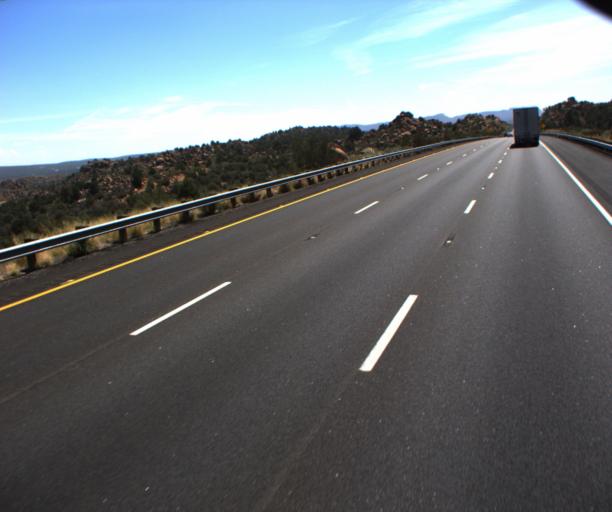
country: US
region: Arizona
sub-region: Mohave County
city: Peach Springs
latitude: 35.1852
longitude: -113.4040
